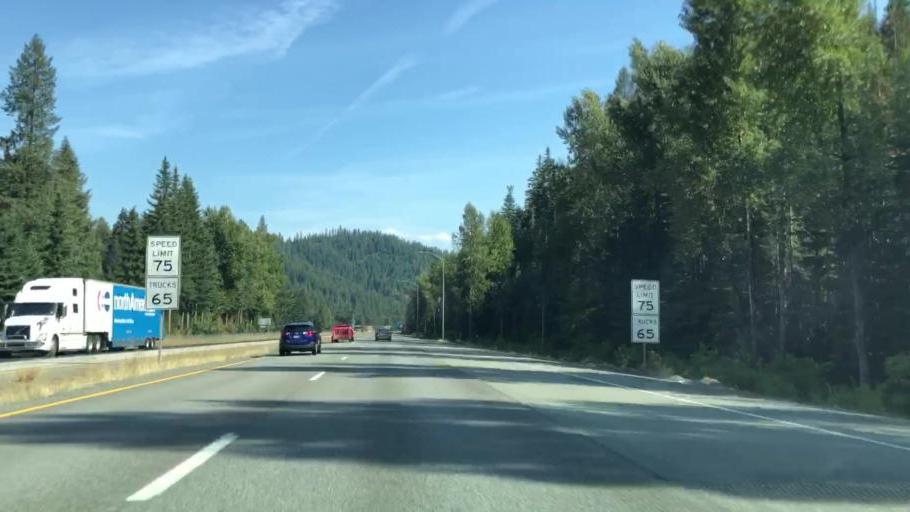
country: US
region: Idaho
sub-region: Shoshone County
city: Pinehurst
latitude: 47.5783
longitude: -116.4554
